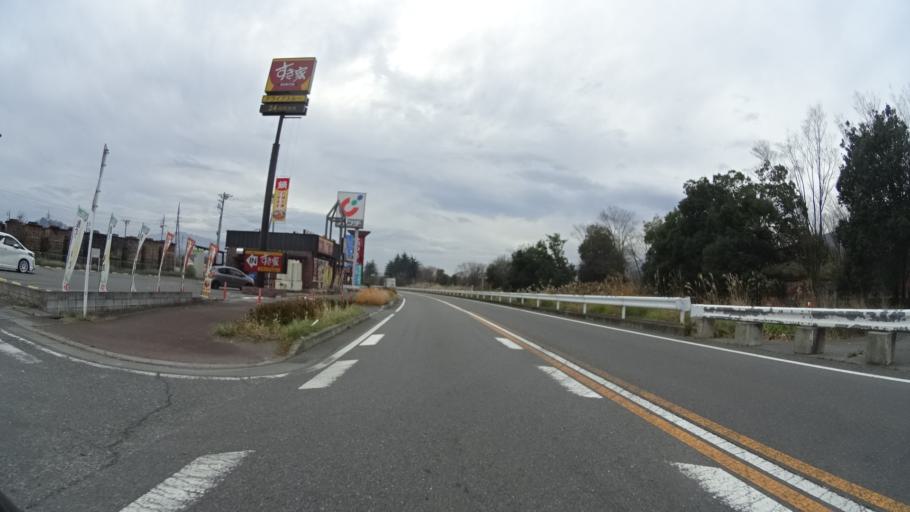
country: JP
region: Gunma
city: Numata
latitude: 36.6521
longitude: 139.0228
